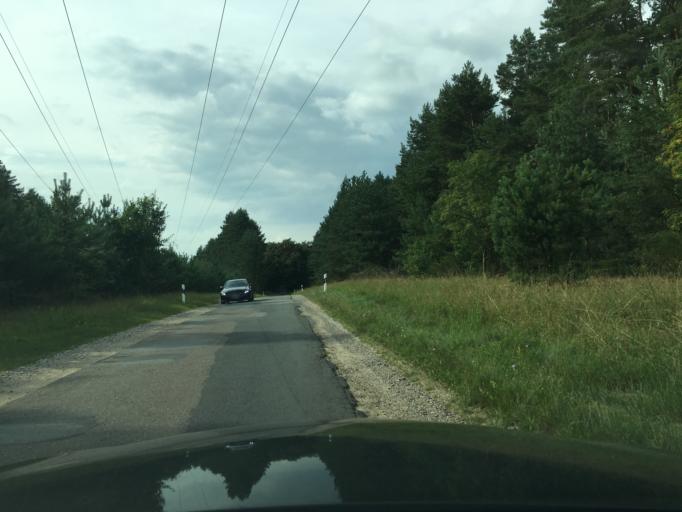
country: DE
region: Mecklenburg-Vorpommern
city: Waren
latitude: 53.4713
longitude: 12.7846
